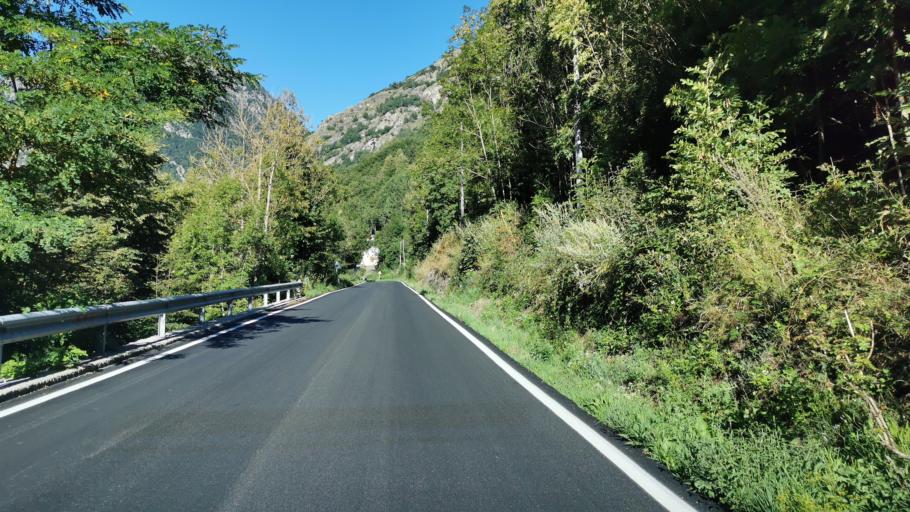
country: IT
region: Piedmont
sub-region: Provincia di Cuneo
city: Entracque
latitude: 44.2501
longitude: 7.3378
